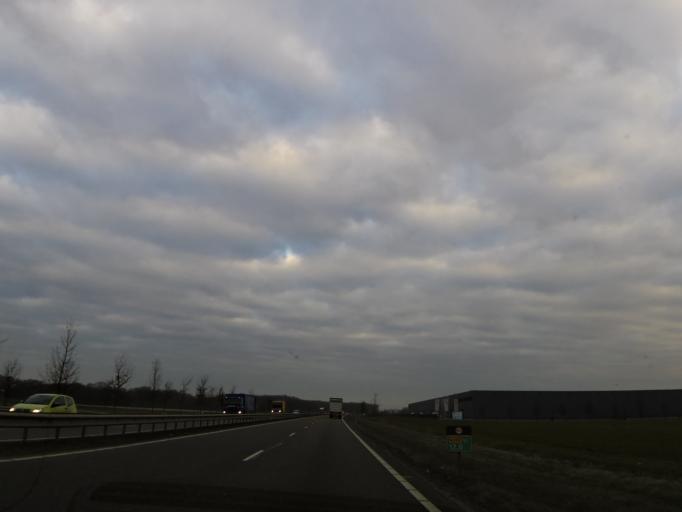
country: NL
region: Limburg
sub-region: Gemeente Sittard-Geleen
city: Limbricht
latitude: 51.0318
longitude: 5.8453
